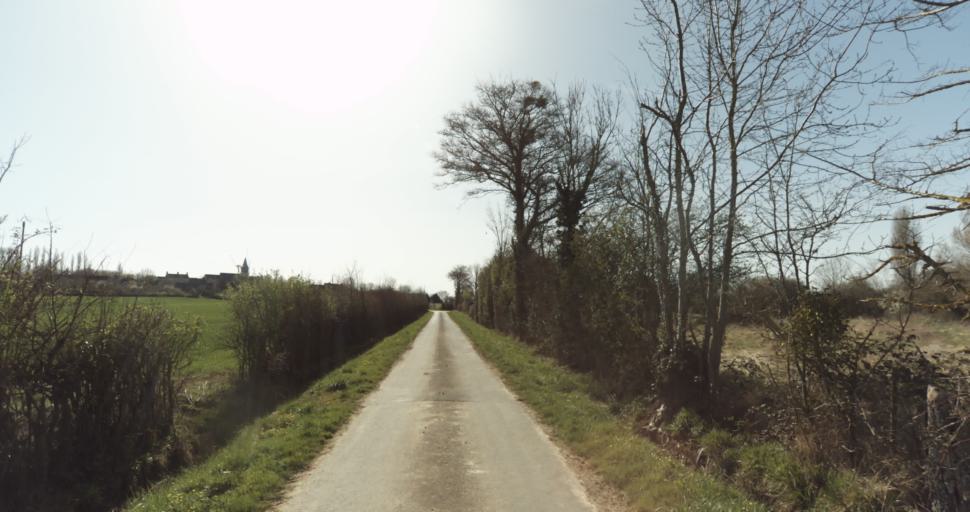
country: FR
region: Lower Normandy
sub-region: Departement du Calvados
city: Saint-Pierre-sur-Dives
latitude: 48.9466
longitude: -0.0034
